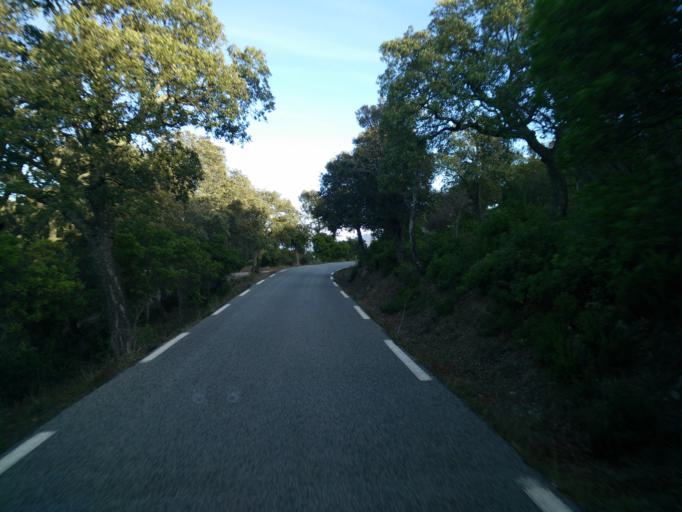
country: FR
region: Provence-Alpes-Cote d'Azur
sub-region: Departement du Var
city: Bormes-les-Mimosas
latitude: 43.1879
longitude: 6.3289
